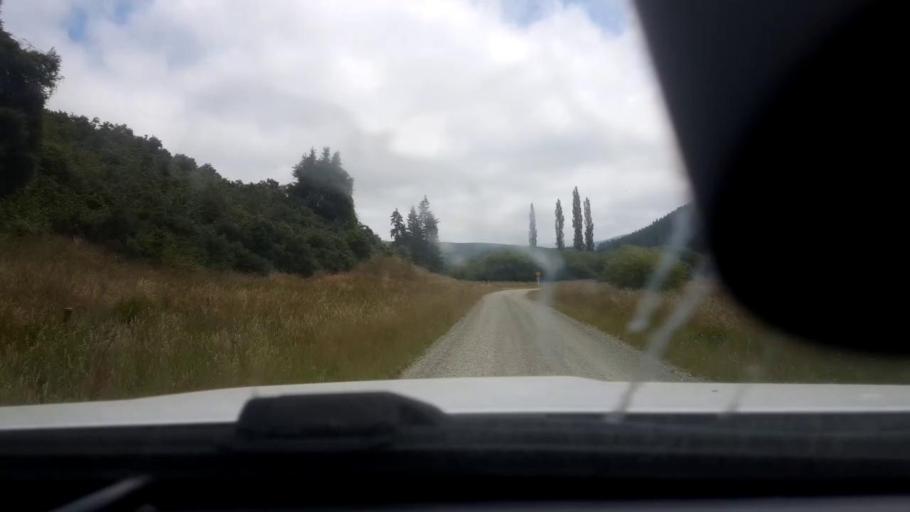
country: NZ
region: Canterbury
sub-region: Timaru District
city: Pleasant Point
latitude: -44.1492
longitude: 171.0887
